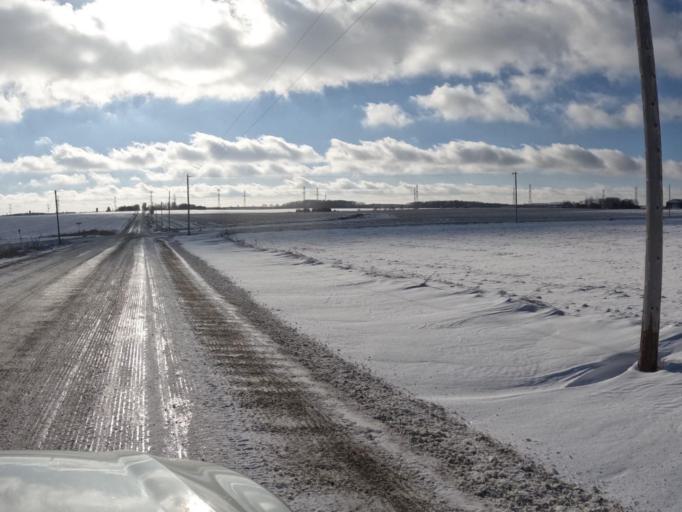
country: CA
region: Ontario
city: Shelburne
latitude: 44.0071
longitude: -80.4110
